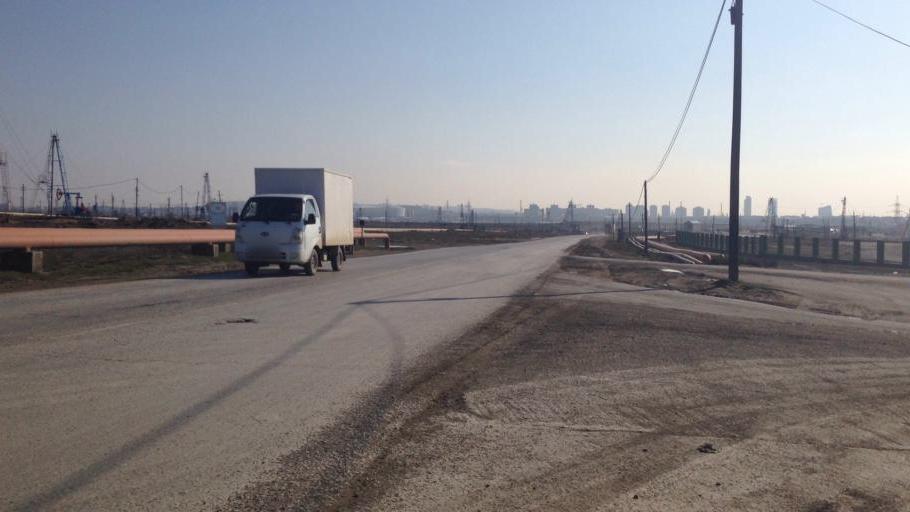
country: AZ
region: Baki
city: Balakhani
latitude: 40.4610
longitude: 49.8900
